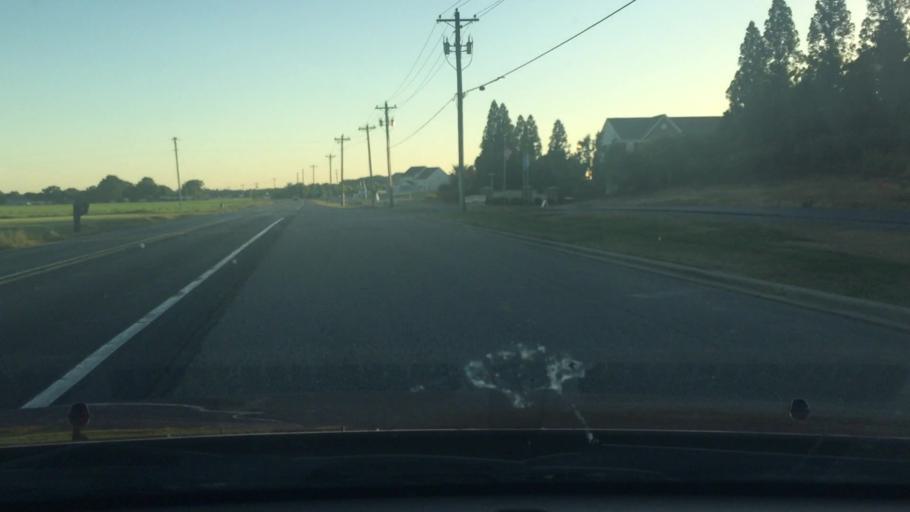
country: US
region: Delaware
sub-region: Kent County
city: Woodside East
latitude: 39.0516
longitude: -75.5211
